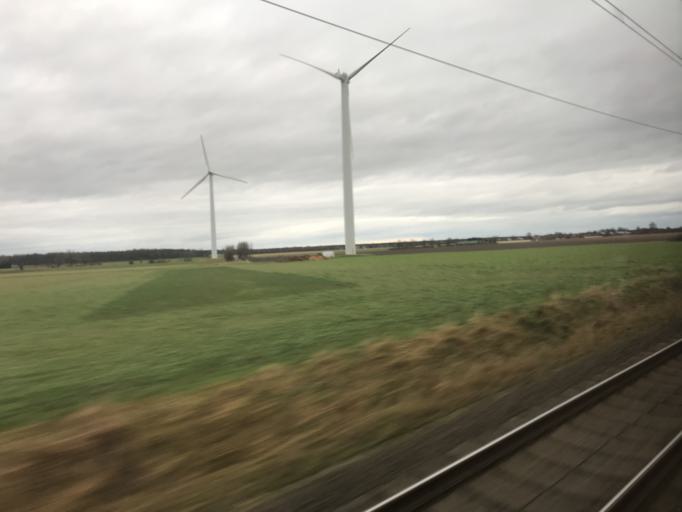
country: DE
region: Lower Saxony
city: Arpke
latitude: 52.3994
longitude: 10.1151
